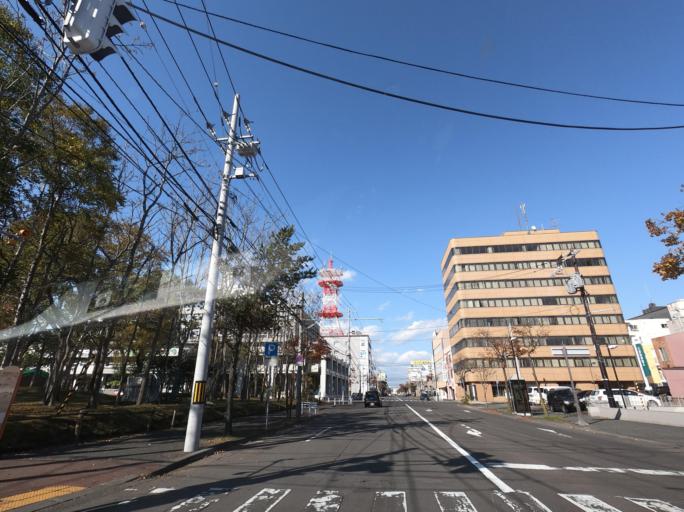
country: JP
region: Hokkaido
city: Kushiro
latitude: 42.9843
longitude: 144.3827
